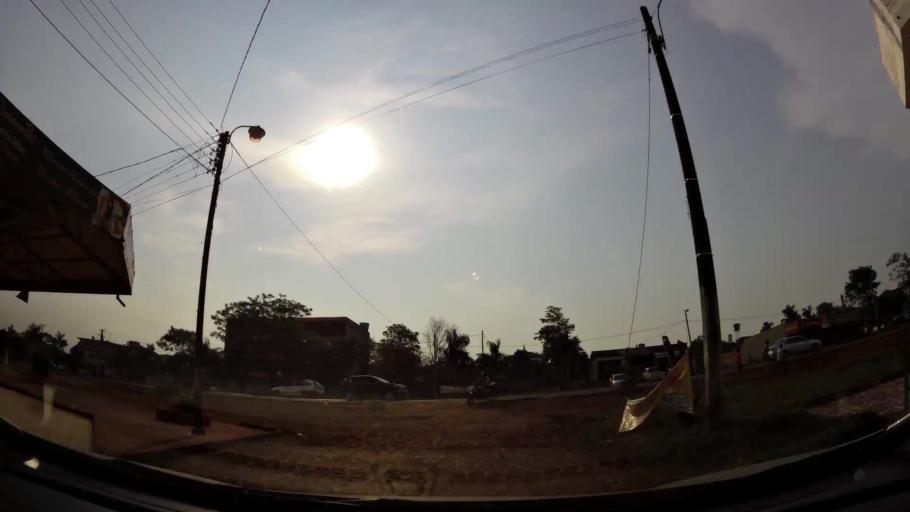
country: PY
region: Alto Parana
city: Ciudad del Este
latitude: -25.4881
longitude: -54.6625
